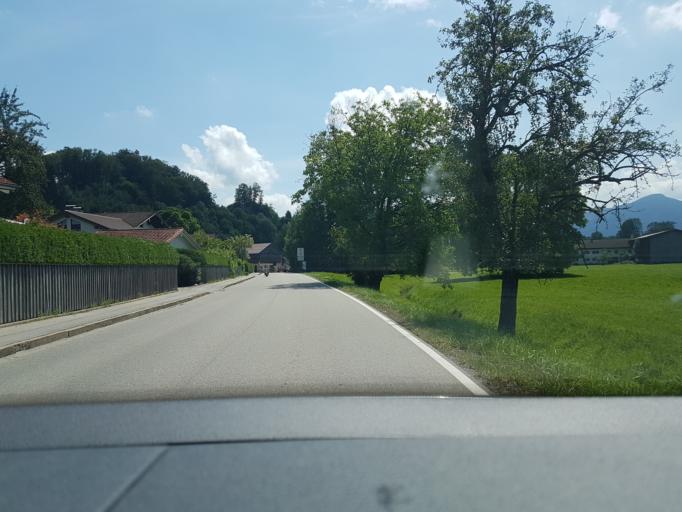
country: DE
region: Bavaria
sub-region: Upper Bavaria
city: Altenmarkt
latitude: 47.7812
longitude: 12.1335
